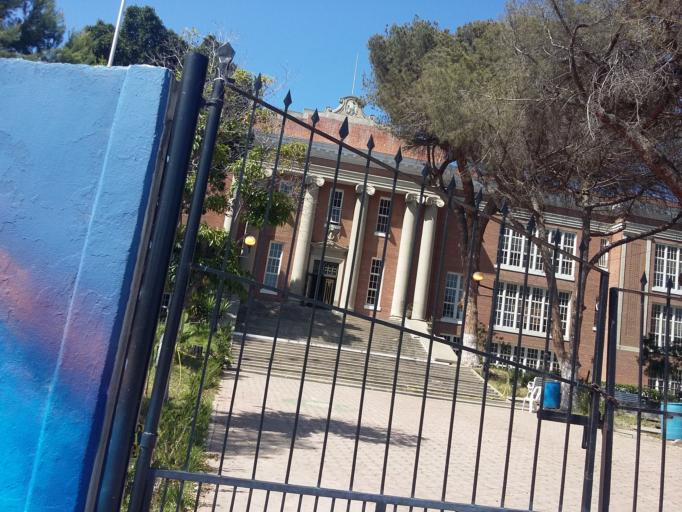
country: MX
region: Baja California
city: Tijuana
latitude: 32.5321
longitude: -117.0516
